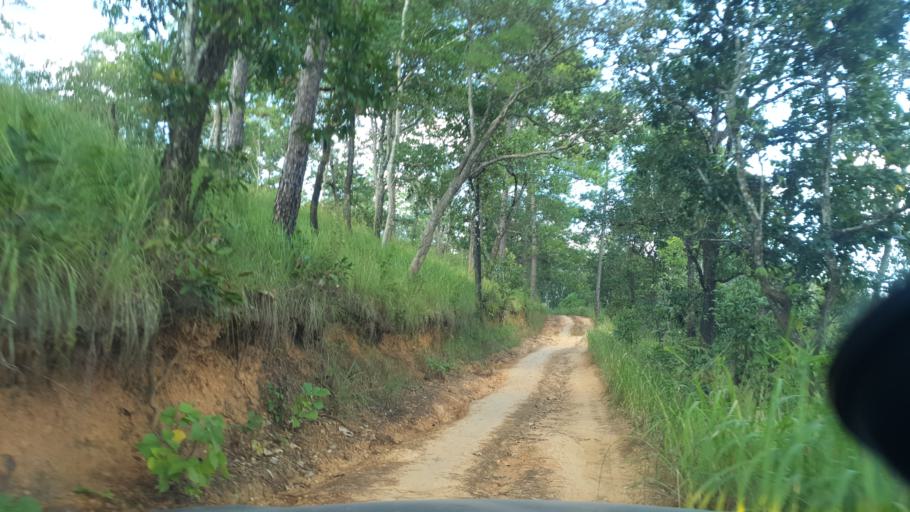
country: TH
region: Chiang Mai
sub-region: Amphoe Chiang Dao
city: Chiang Dao
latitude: 19.4113
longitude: 98.8323
